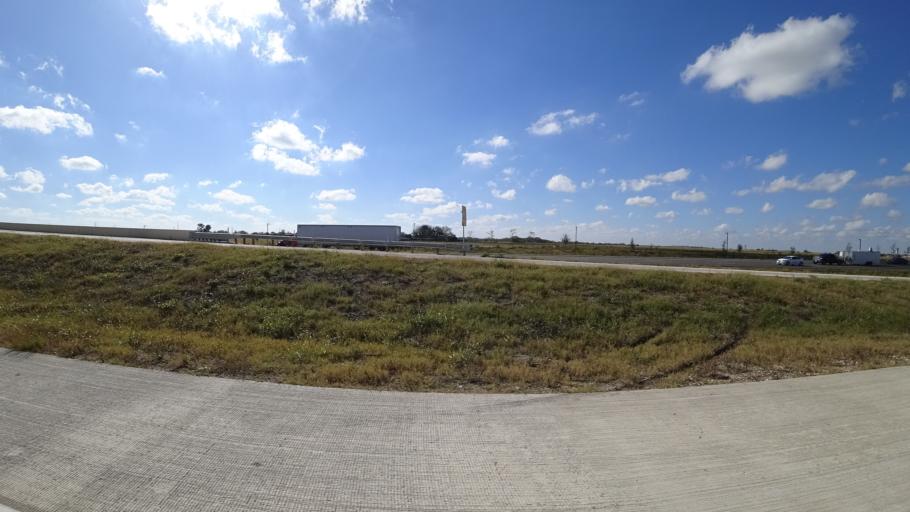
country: US
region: Texas
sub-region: Travis County
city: Hornsby Bend
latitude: 30.1985
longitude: -97.6309
